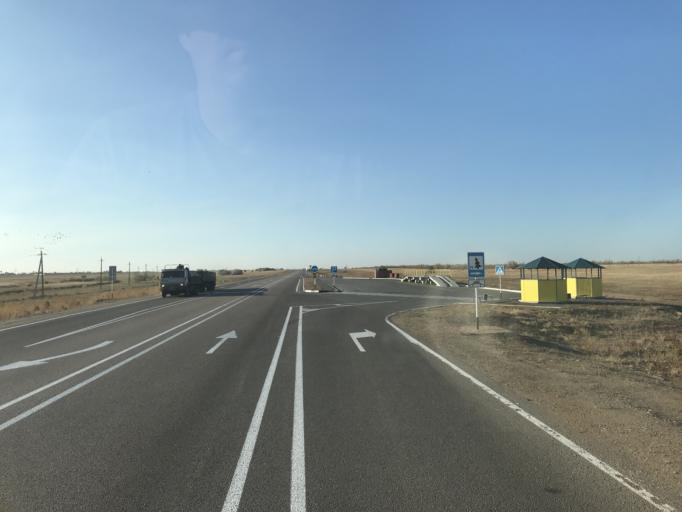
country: KZ
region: Pavlodar
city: Koktobe
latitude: 51.8822
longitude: 77.4197
